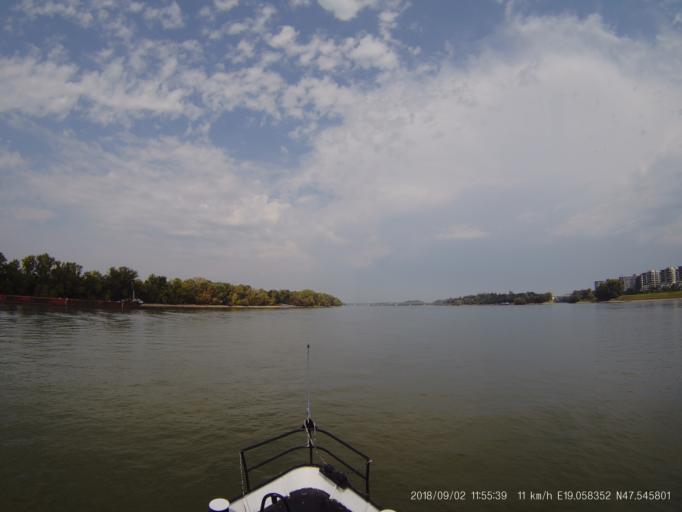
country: HU
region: Budapest
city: Budapest III. keruelet
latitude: 47.5433
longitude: 19.0579
